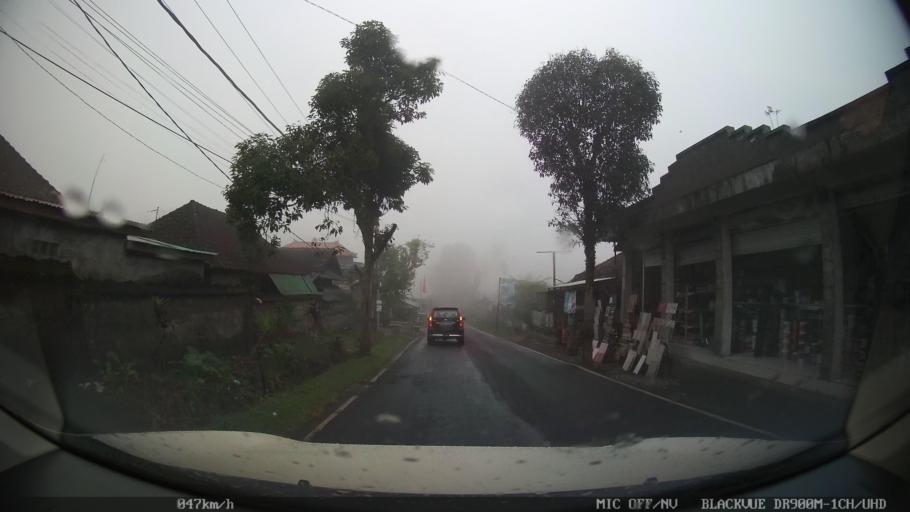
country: ID
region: Bali
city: Banjar Taro Kelod
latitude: -8.3403
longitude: 115.2817
